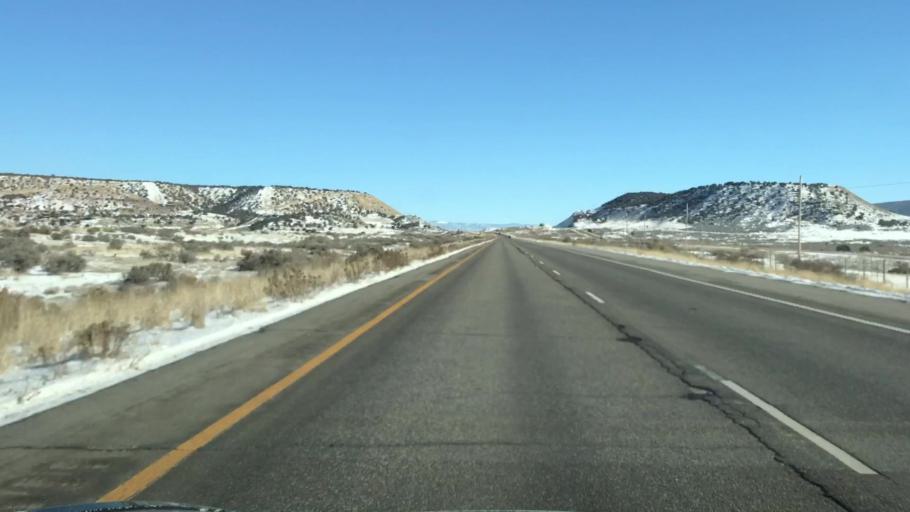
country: US
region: Colorado
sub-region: Garfield County
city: Rifle
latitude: 39.5038
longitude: -107.8976
